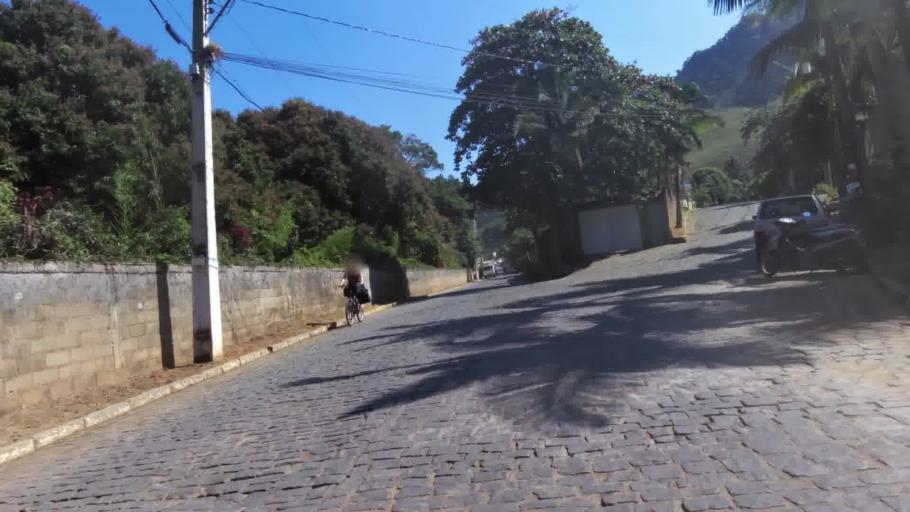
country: BR
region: Espirito Santo
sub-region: Alfredo Chaves
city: Alfredo Chaves
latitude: -20.6305
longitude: -40.7630
